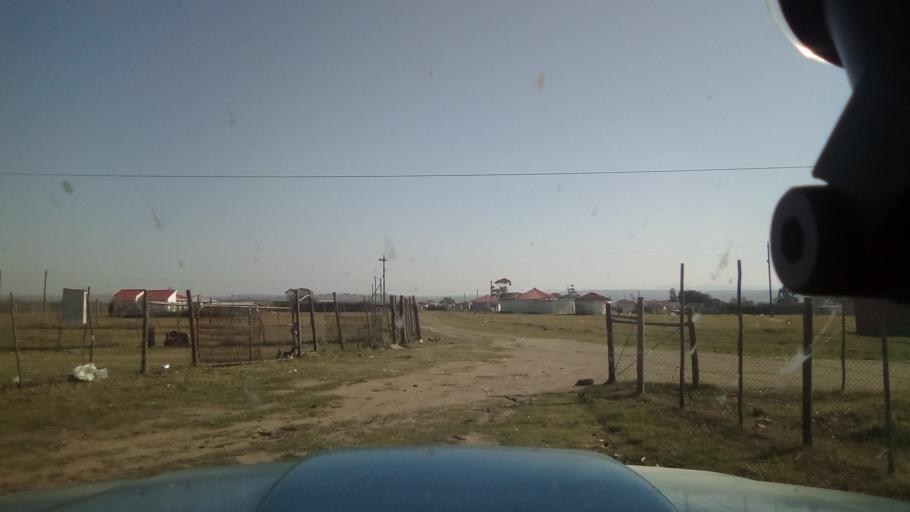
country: ZA
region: Eastern Cape
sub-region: Buffalo City Metropolitan Municipality
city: Bhisho
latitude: -32.9433
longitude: 27.3364
